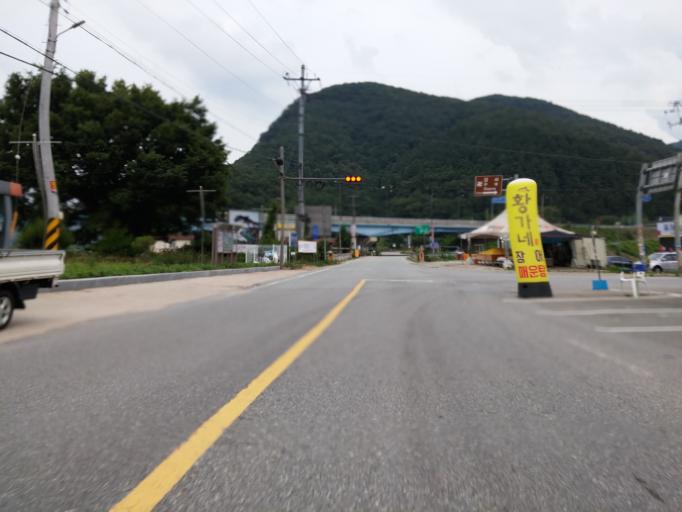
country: KR
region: Chungcheongnam-do
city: Gongju
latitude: 36.4343
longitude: 127.2100
